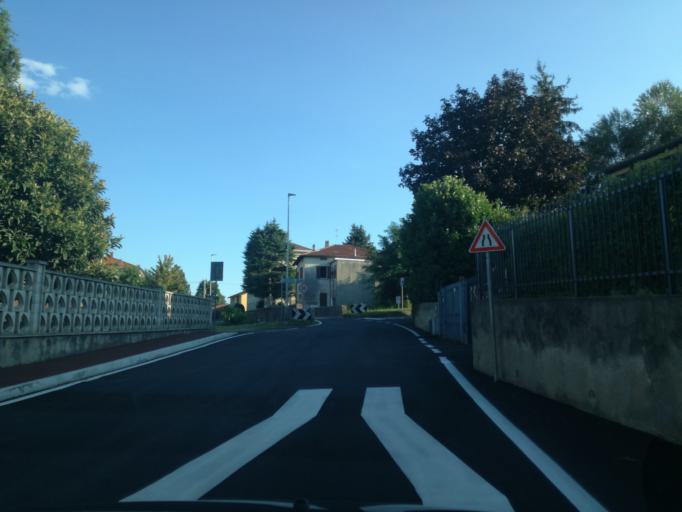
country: IT
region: Lombardy
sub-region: Provincia di Lecco
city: Paderno d'Adda
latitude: 45.6803
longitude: 9.4470
